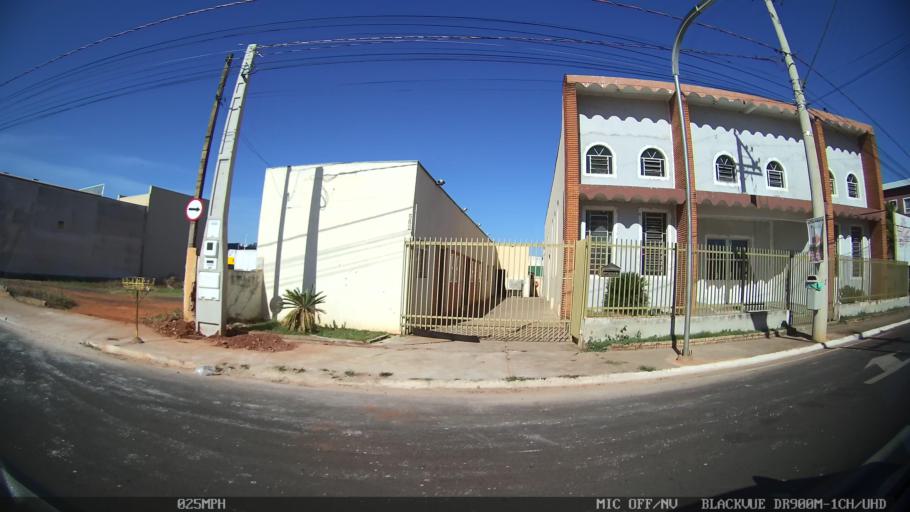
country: BR
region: Sao Paulo
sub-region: Olimpia
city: Olimpia
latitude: -20.7301
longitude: -48.9153
